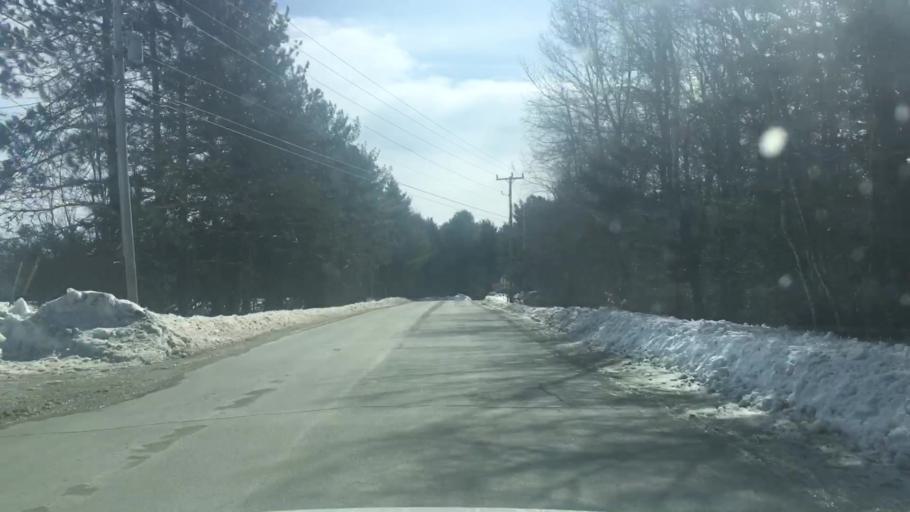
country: US
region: Maine
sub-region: Penobscot County
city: Holden
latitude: 44.7677
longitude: -68.6476
